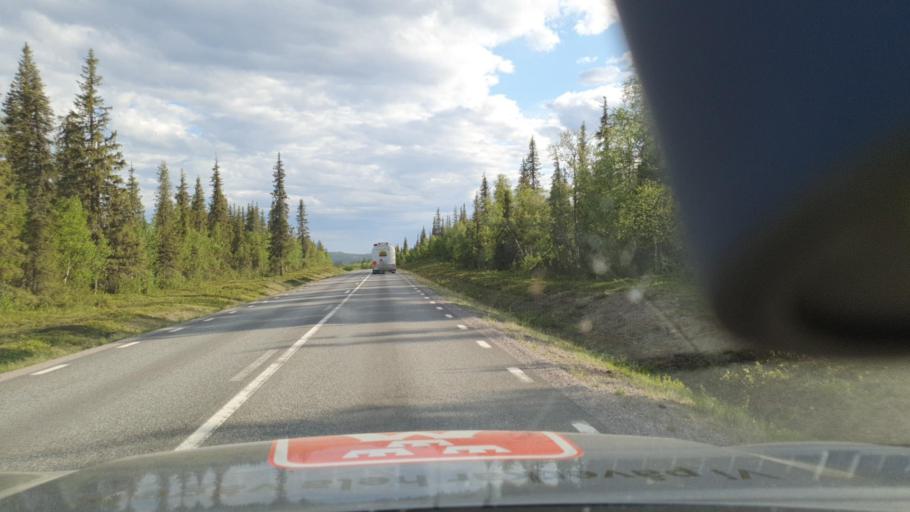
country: SE
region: Norrbotten
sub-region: Gallivare Kommun
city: Malmberget
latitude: 67.2669
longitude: 21.0345
